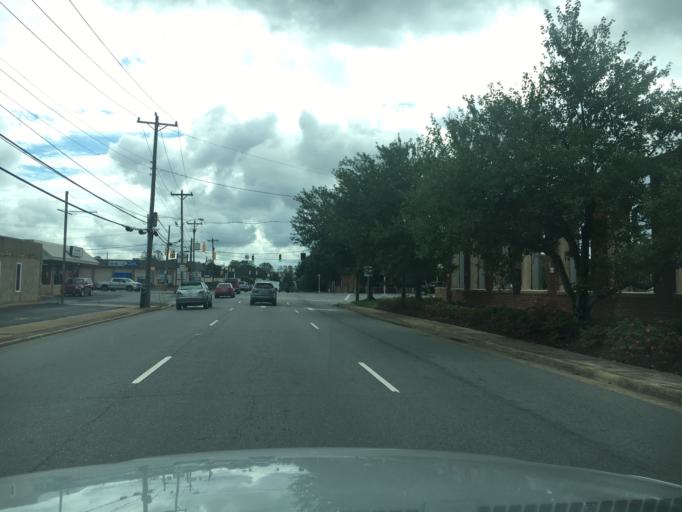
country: US
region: North Carolina
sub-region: Catawba County
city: Hickory
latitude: 35.7388
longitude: -81.3102
